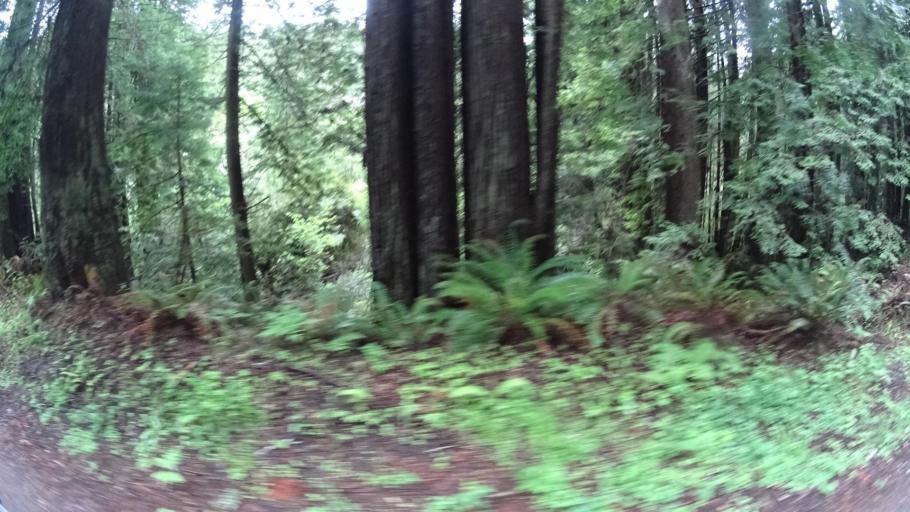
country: US
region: California
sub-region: Humboldt County
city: Bayside
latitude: 40.8202
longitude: -124.0305
